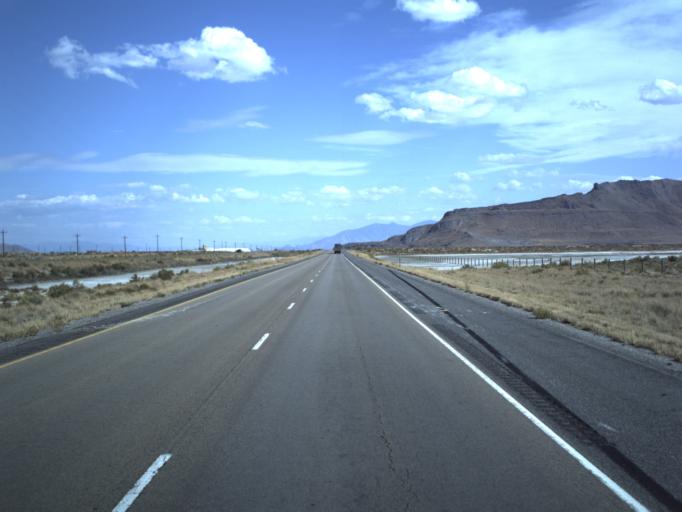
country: US
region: Utah
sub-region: Tooele County
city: Grantsville
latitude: 40.7500
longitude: -112.6969
